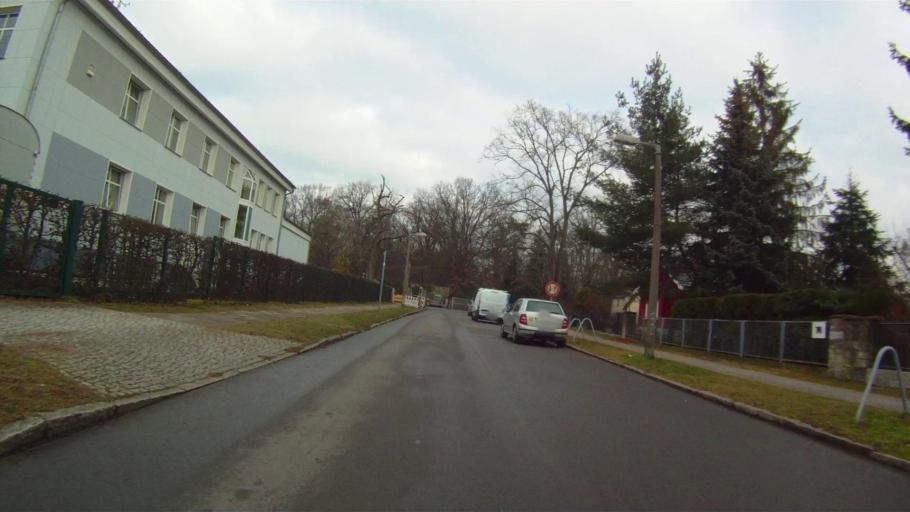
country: DE
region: Berlin
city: Karlshorst
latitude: 52.4920
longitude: 13.5334
